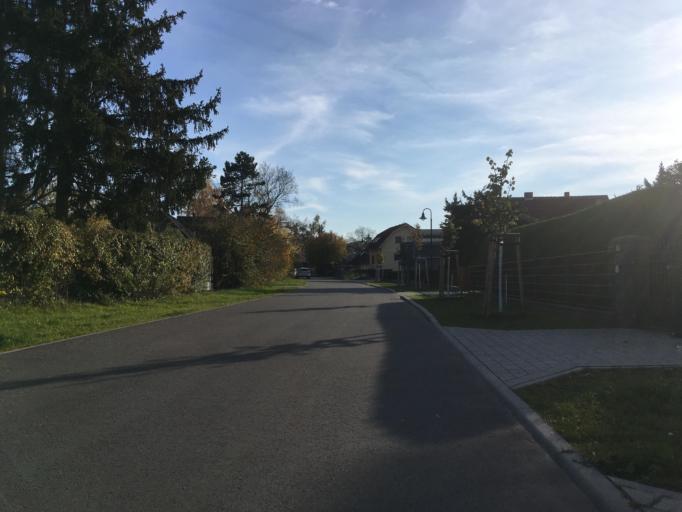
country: DE
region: Berlin
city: Buch
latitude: 52.6461
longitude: 13.5408
